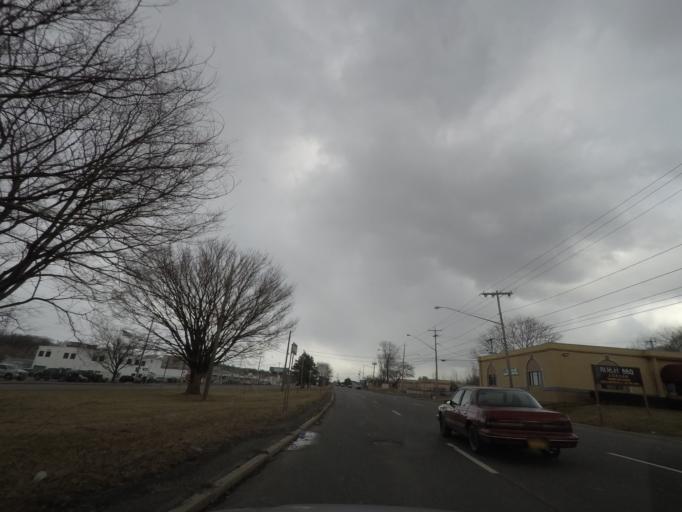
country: US
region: New York
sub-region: Onondaga County
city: Lyncourt
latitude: 43.0516
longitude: -76.1134
